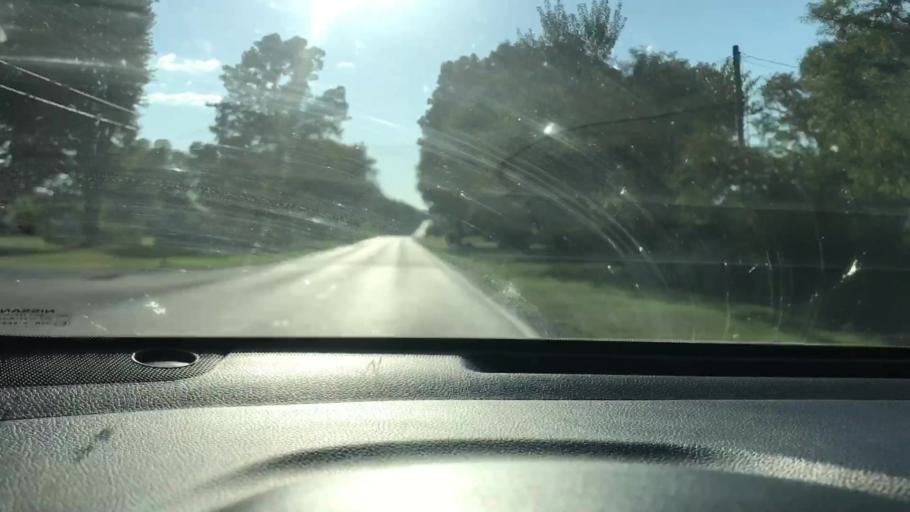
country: US
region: Kentucky
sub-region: Calloway County
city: Murray
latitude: 36.5805
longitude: -88.2471
